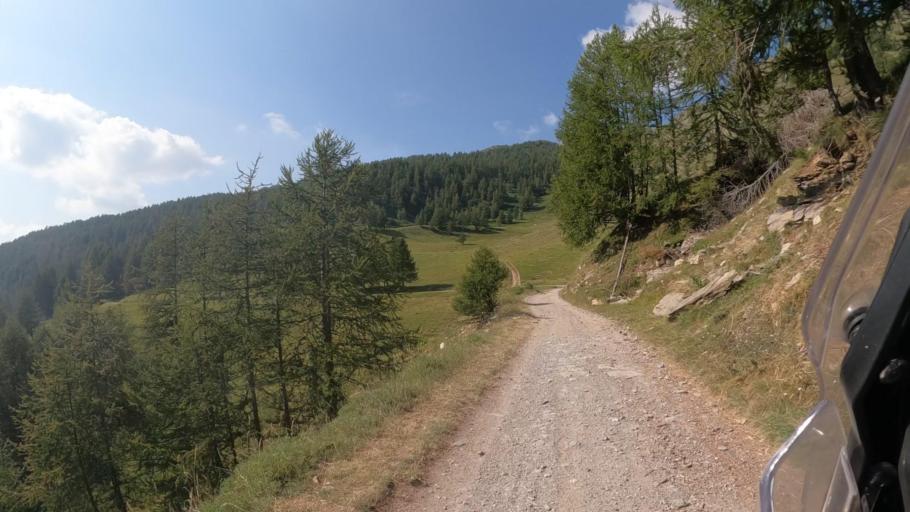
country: IT
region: Piedmont
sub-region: Provincia di Cuneo
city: Briga Alta
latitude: 44.0911
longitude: 7.7205
